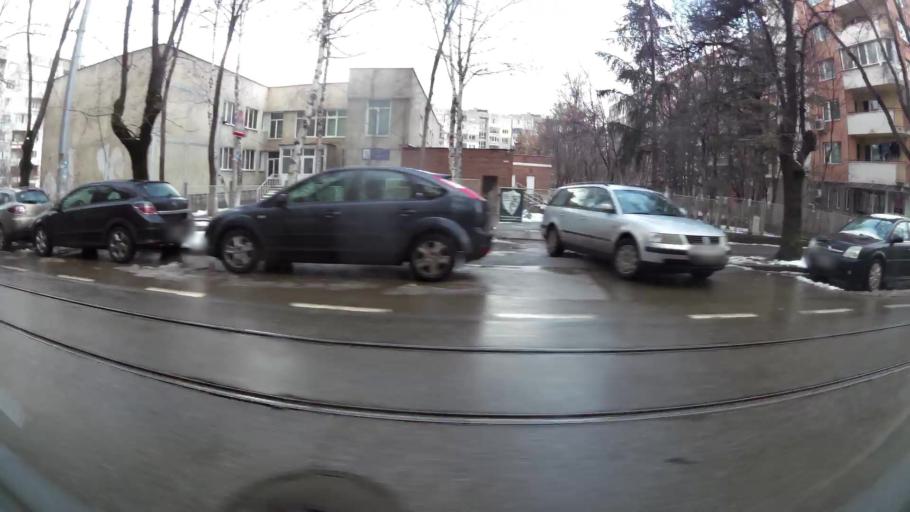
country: BG
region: Sofia-Capital
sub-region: Stolichna Obshtina
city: Sofia
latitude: 42.7081
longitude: 23.2892
